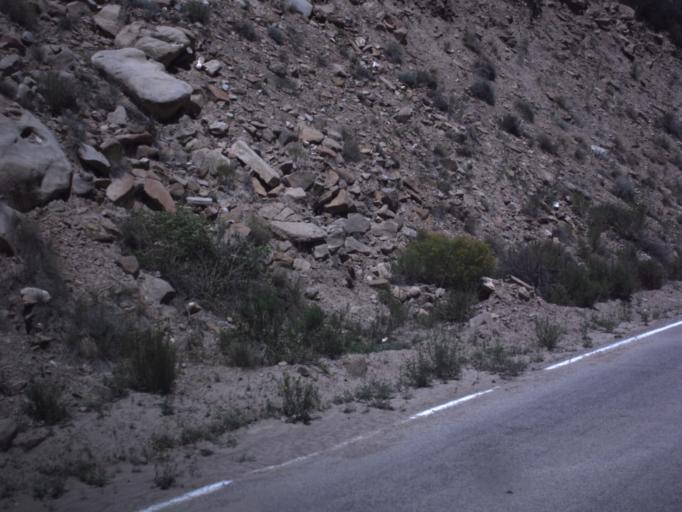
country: US
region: Utah
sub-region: Emery County
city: Orangeville
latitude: 39.2729
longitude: -111.1971
